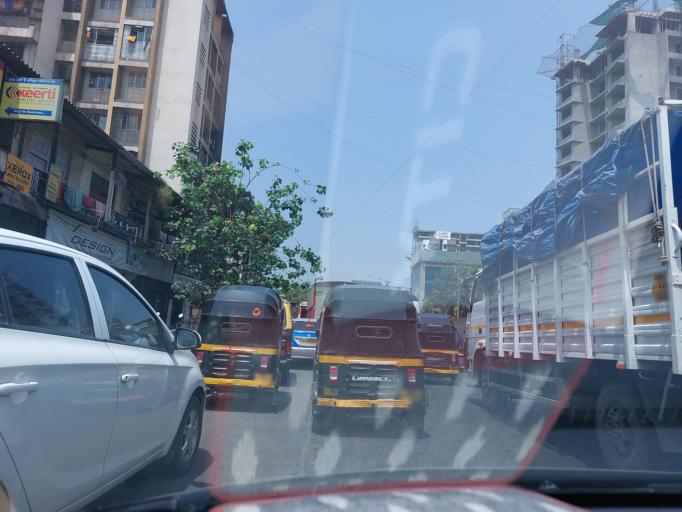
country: IN
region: Maharashtra
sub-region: Mumbai Suburban
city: Mumbai
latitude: 19.0541
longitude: 72.8917
